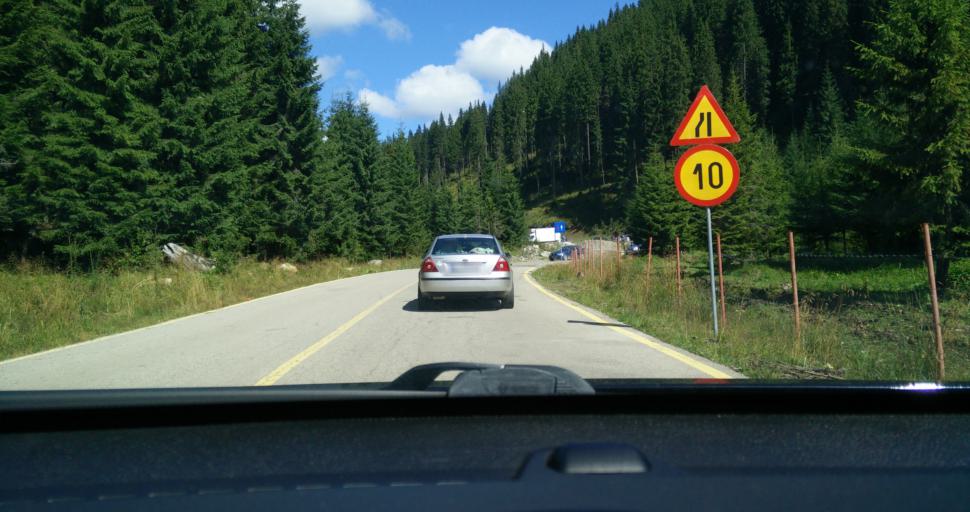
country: RO
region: Hunedoara
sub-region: Oras Petrila
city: Petrila
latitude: 45.4374
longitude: 23.6295
